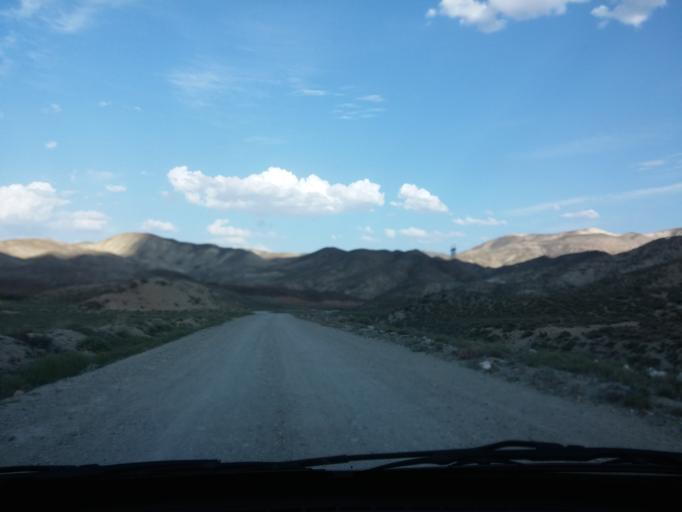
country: IR
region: Tehran
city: Damavand
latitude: 35.5322
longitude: 52.2353
